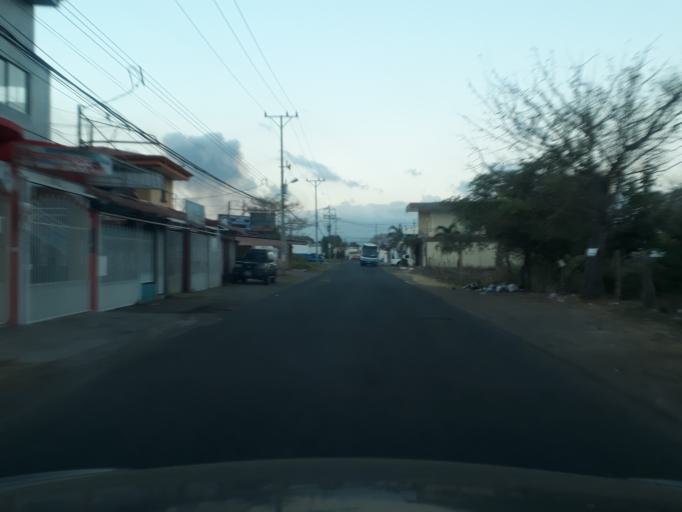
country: CR
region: Puntarenas
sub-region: Canton Central de Puntarenas
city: Chacarita
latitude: 9.9762
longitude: -84.7519
